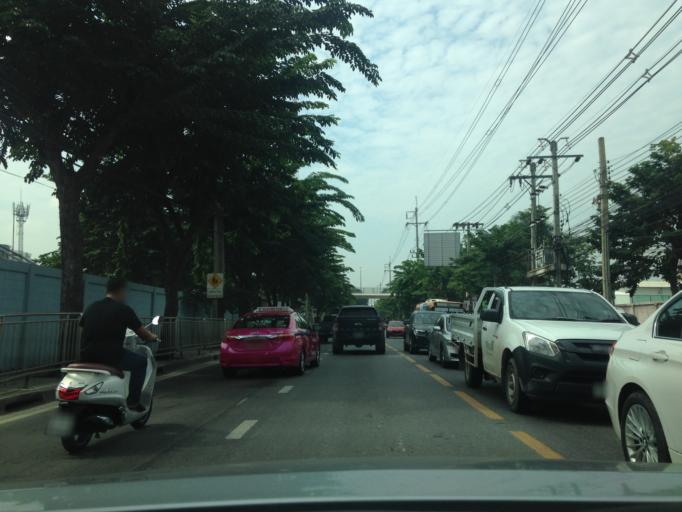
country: TH
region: Bangkok
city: Bang Phlat
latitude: 13.7967
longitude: 100.5208
